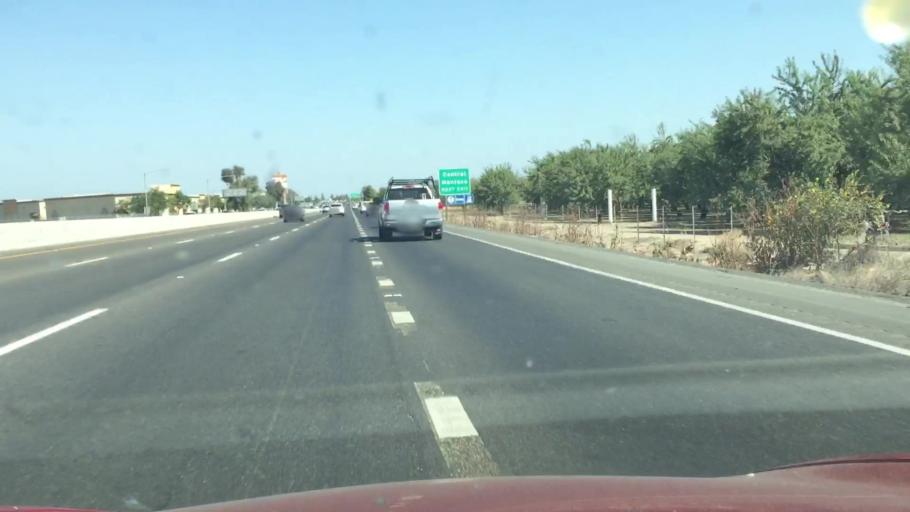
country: US
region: California
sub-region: San Joaquin County
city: Manteca
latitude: 37.7883
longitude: -121.1888
